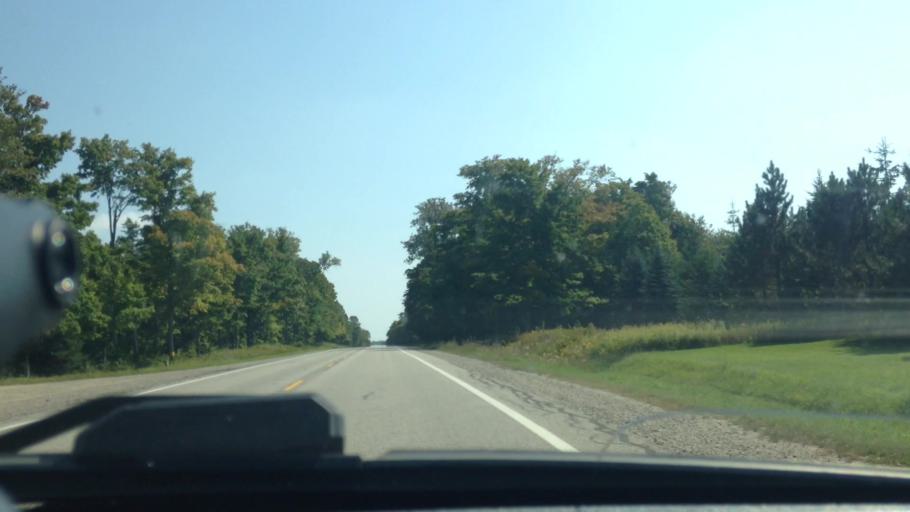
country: US
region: Michigan
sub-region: Luce County
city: Newberry
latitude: 46.3237
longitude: -85.6700
